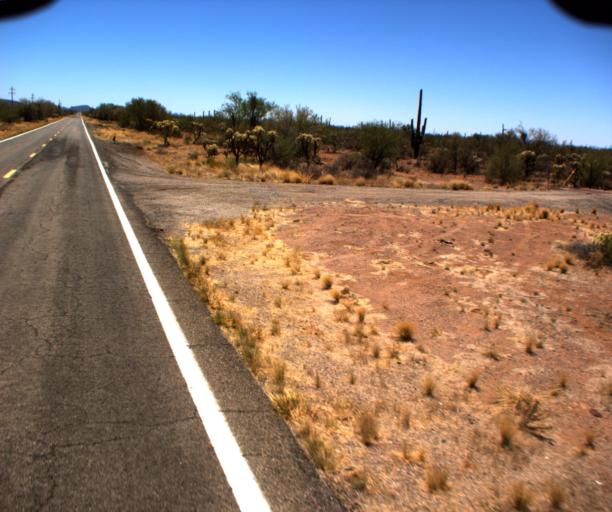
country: US
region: Arizona
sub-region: Pima County
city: Sells
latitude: 32.0498
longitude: -112.0252
